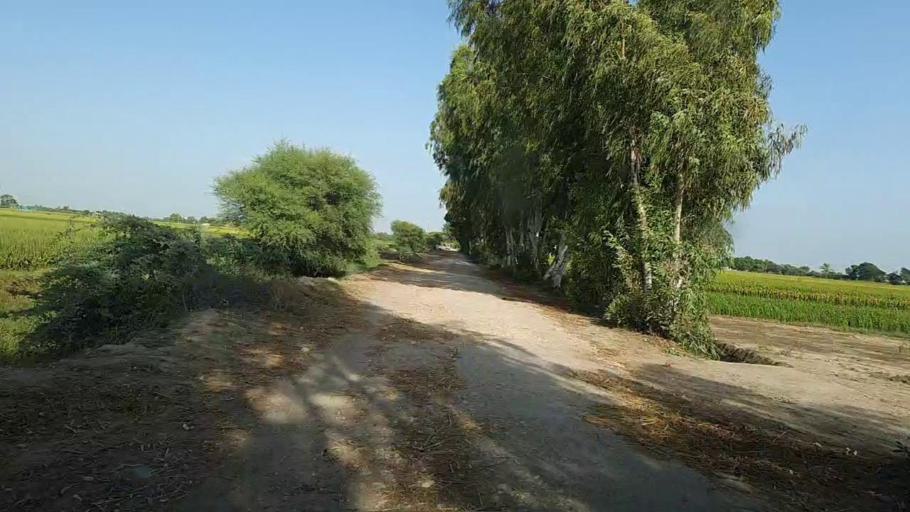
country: PK
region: Sindh
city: Kario
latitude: 24.5996
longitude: 68.5181
